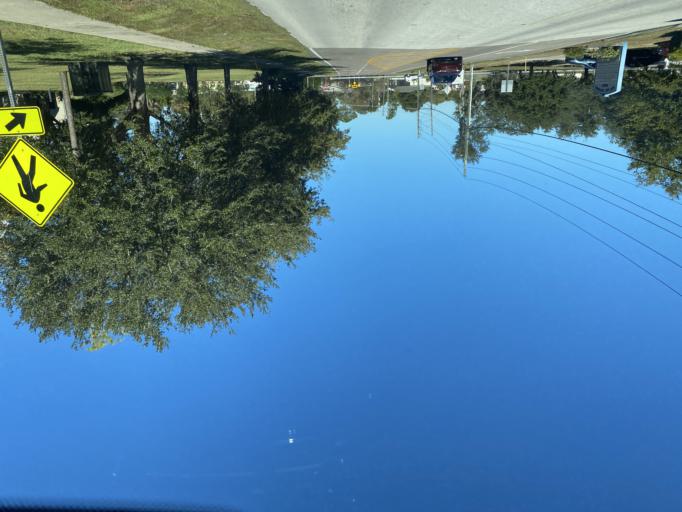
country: US
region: Florida
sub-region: Sumter County
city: The Villages
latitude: 28.9367
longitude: -81.9369
